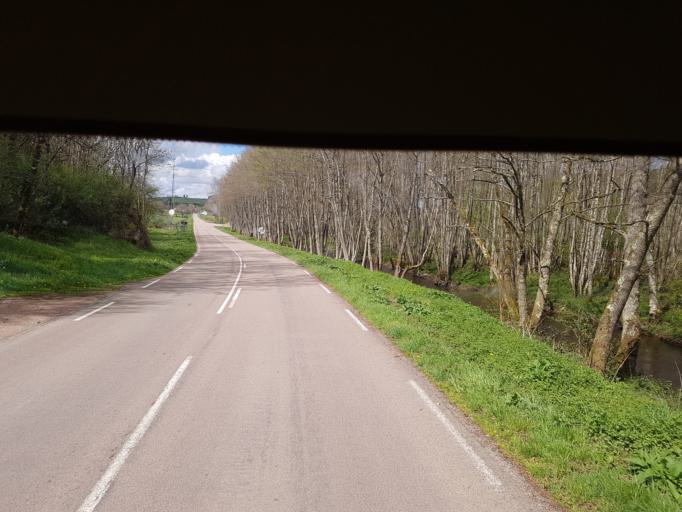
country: FR
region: Bourgogne
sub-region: Departement de Saone-et-Loire
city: Autun
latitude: 47.1036
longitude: 4.2306
